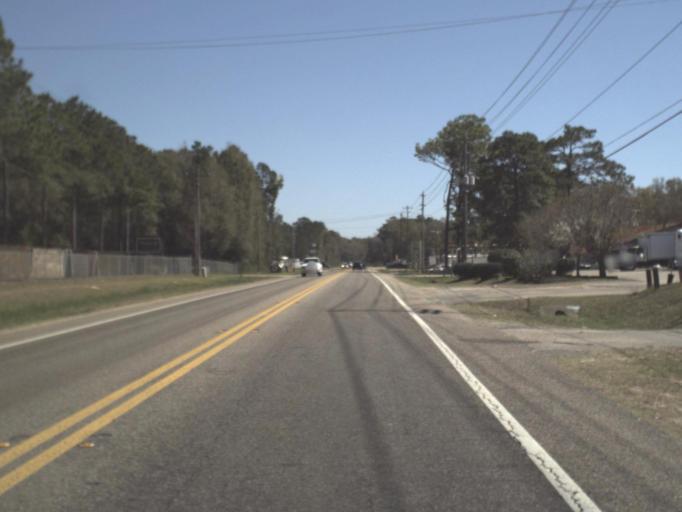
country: US
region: Florida
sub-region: Leon County
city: Tallahassee
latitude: 30.3811
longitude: -84.3045
